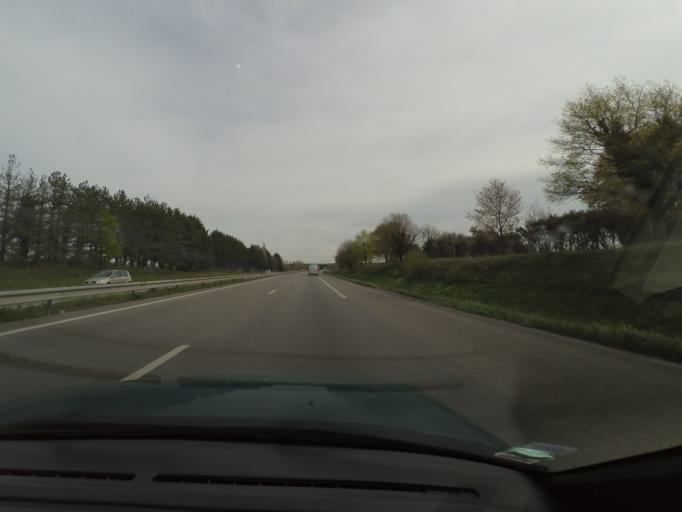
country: FR
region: Pays de la Loire
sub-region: Departement de la Loire-Atlantique
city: Mauves-sur-Loire
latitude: 47.3254
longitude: -1.4050
